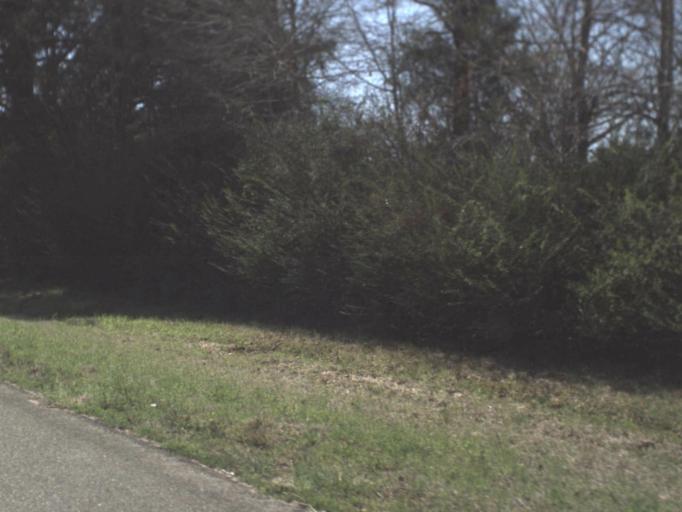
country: US
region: Florida
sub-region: Calhoun County
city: Blountstown
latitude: 30.5183
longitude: -85.0313
